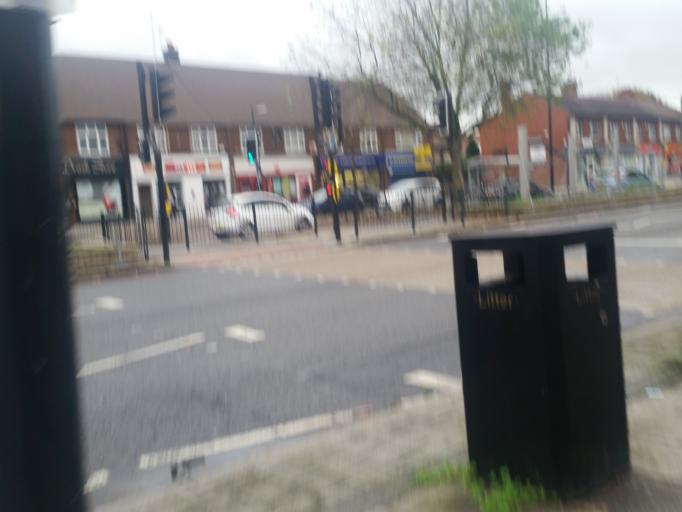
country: GB
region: England
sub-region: Derbyshire
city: Borrowash
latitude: 52.8966
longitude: -1.4285
